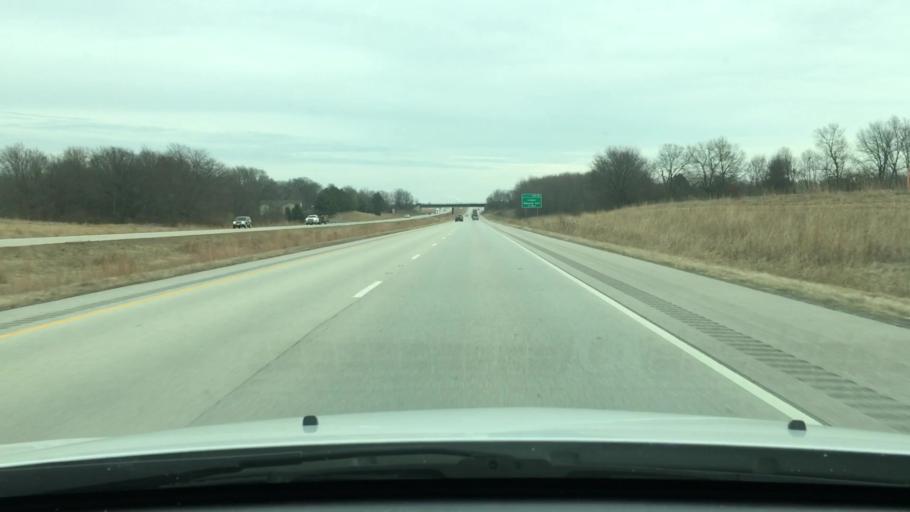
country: US
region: Illinois
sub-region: Sangamon County
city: Jerome
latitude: 39.7517
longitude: -89.7693
